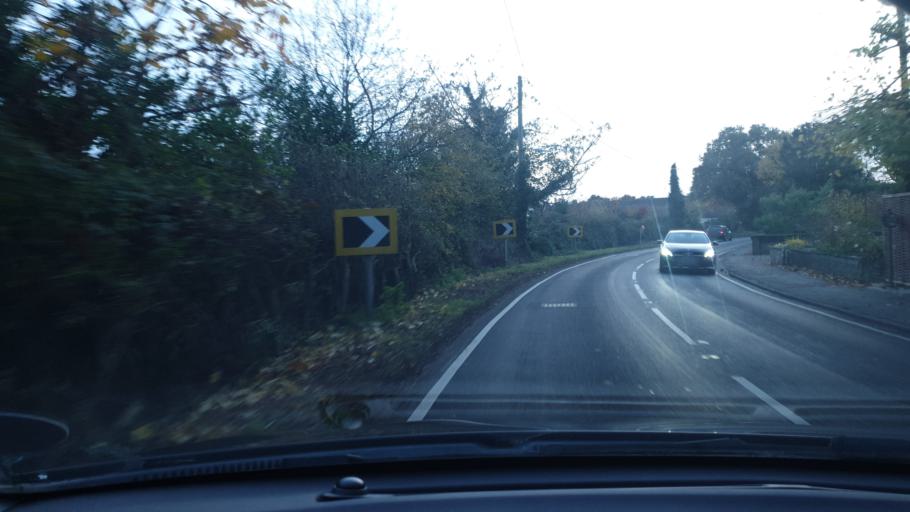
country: GB
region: England
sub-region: Essex
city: Dovercourt
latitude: 51.9193
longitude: 1.2313
